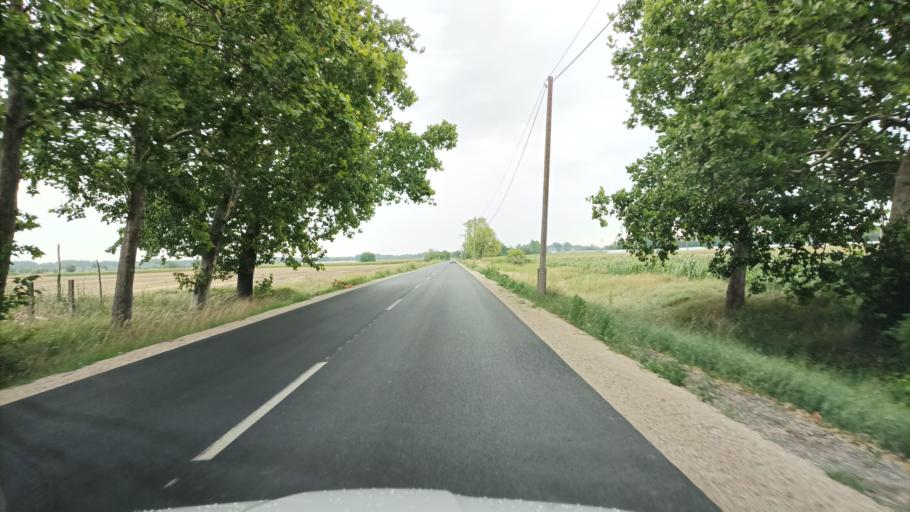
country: HU
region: Pest
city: Dabas
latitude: 47.1936
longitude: 19.2525
